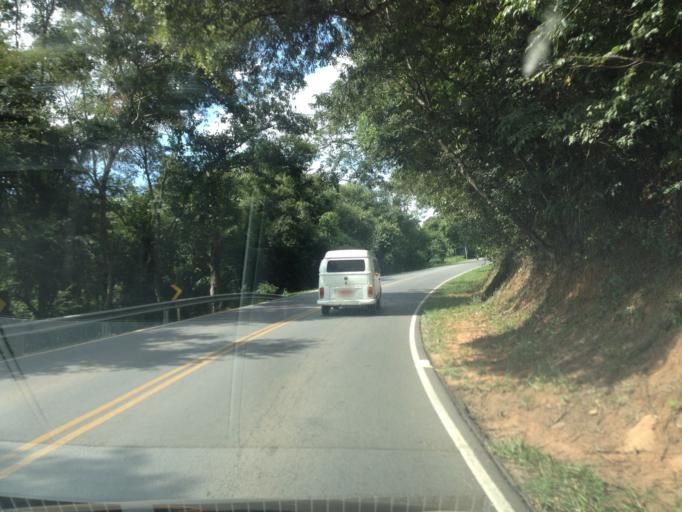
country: BR
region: Minas Gerais
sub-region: Itanhandu
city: Itanhandu
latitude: -22.2043
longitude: -44.9603
